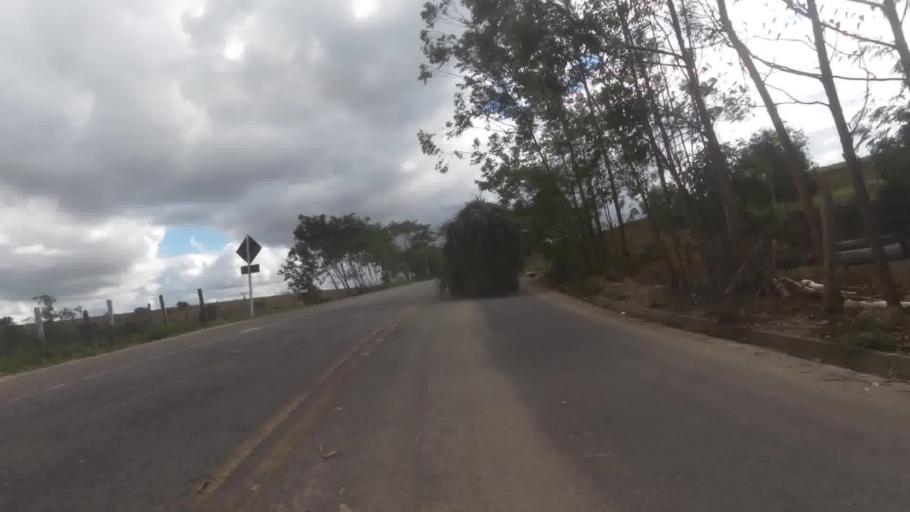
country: BR
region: Espirito Santo
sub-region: Marataizes
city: Marataizes
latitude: -21.2002
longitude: -40.9693
